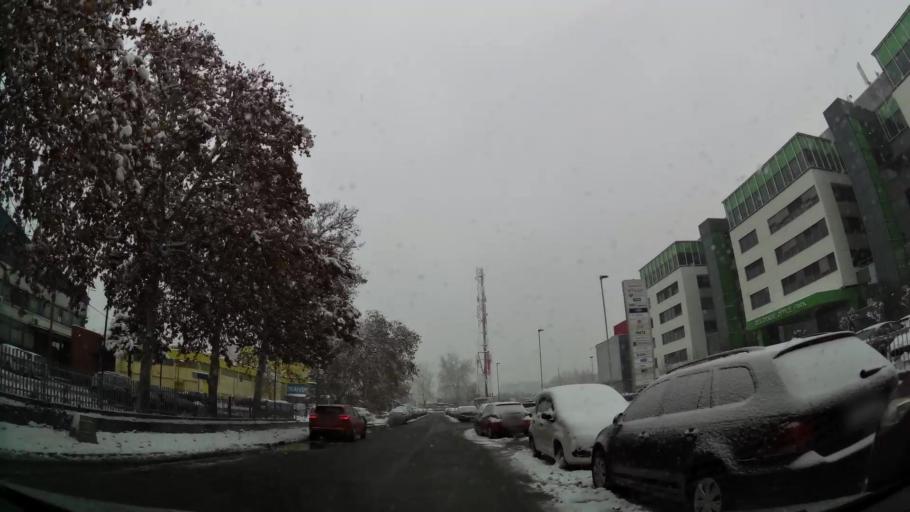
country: RS
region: Central Serbia
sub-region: Belgrade
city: Novi Beograd
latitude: 44.8103
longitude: 20.4041
